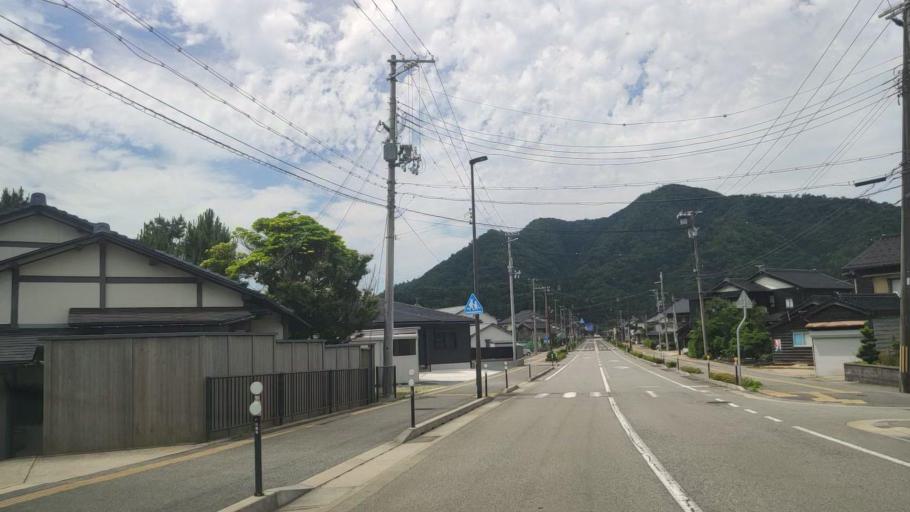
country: JP
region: Hyogo
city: Toyooka
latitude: 35.6533
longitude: 134.7600
